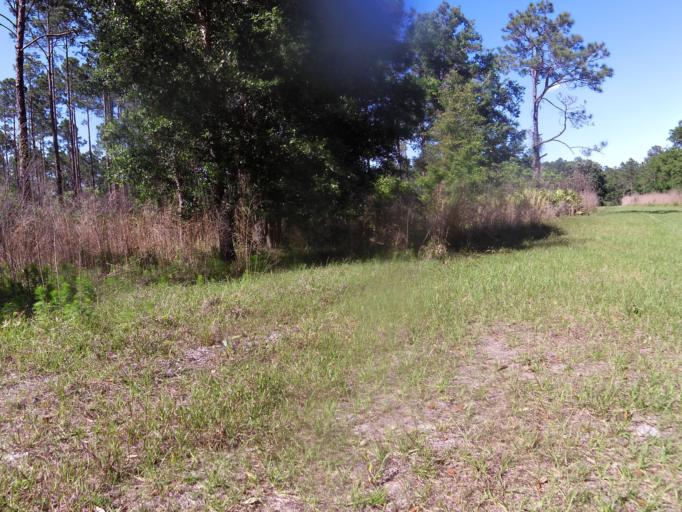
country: US
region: Florida
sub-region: Clay County
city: Green Cove Springs
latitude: 29.9583
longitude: -81.6159
